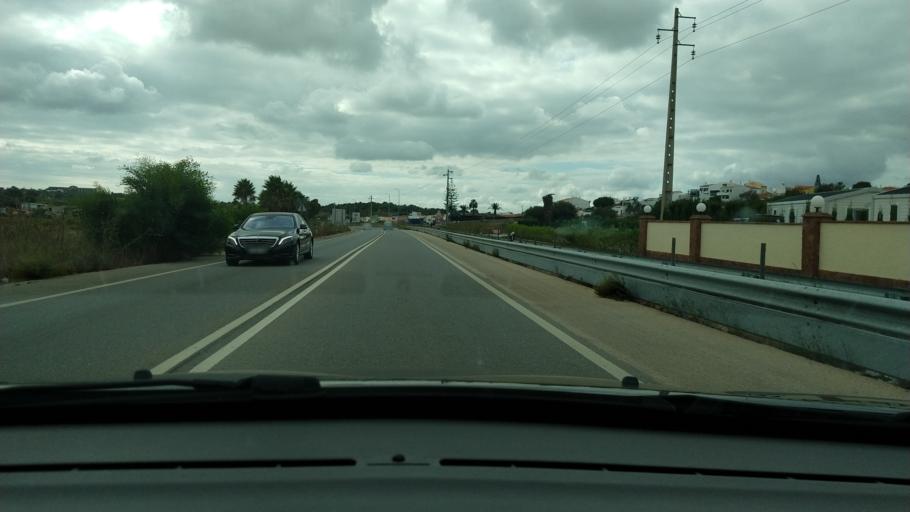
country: PT
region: Faro
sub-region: Lagos
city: Lagos
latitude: 37.1007
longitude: -8.7332
